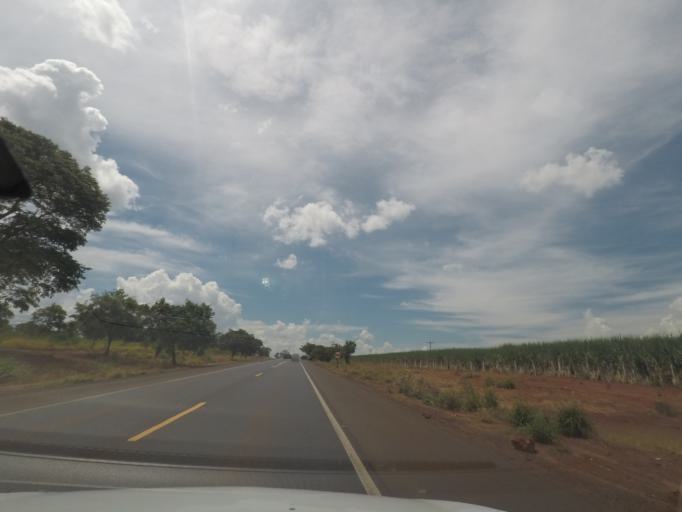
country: BR
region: Sao Paulo
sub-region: Barretos
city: Barretos
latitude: -20.2838
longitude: -48.6707
